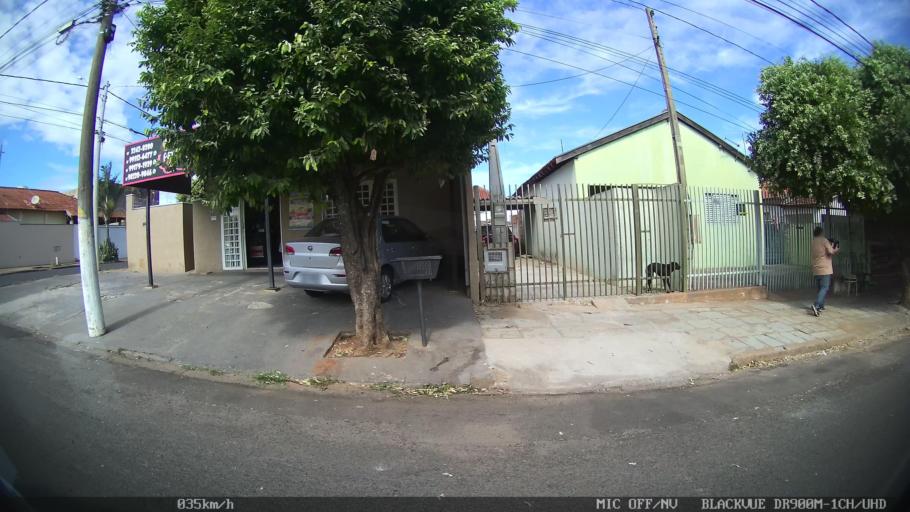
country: BR
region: Sao Paulo
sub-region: Bady Bassitt
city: Bady Bassitt
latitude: -20.8152
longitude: -49.5204
